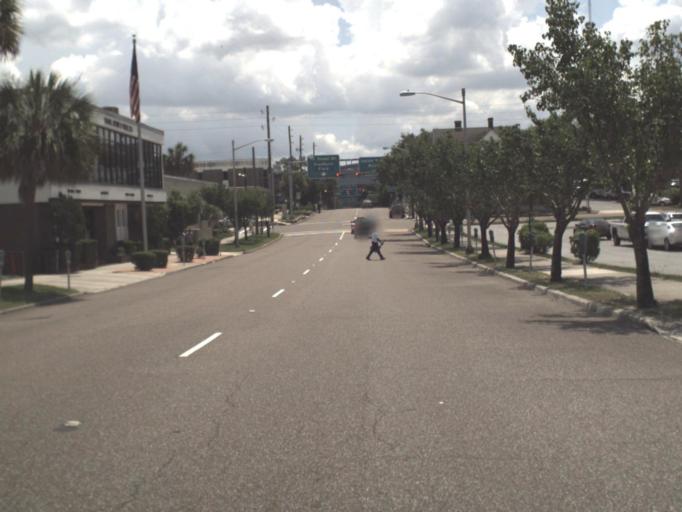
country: US
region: Florida
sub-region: Duval County
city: Jacksonville
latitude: 30.3276
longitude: -81.6533
